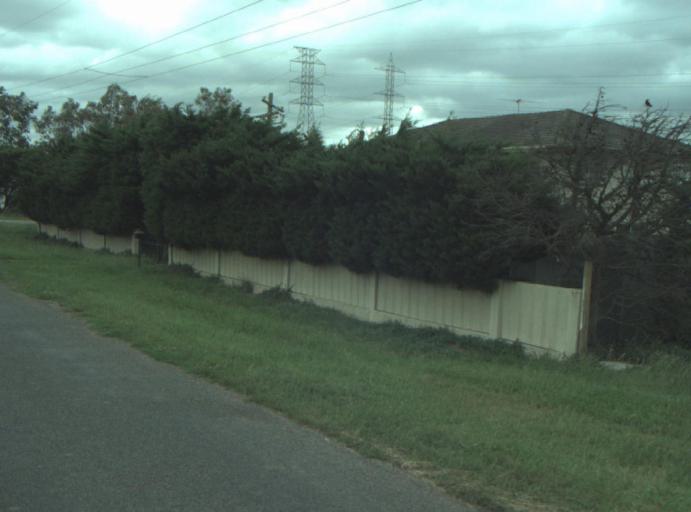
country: AU
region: Victoria
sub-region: Greater Geelong
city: Bell Post Hill
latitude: -38.0546
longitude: 144.3423
